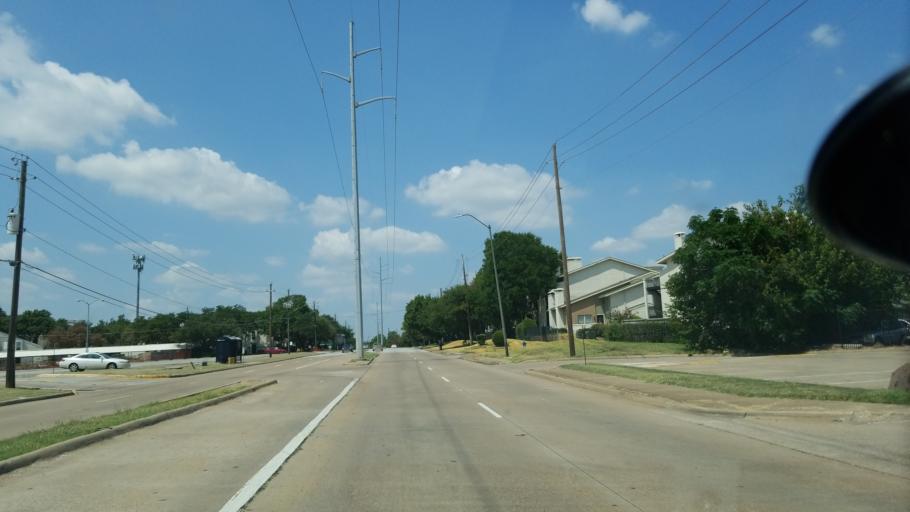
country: US
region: Texas
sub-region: Dallas County
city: Richardson
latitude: 32.9237
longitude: -96.7197
